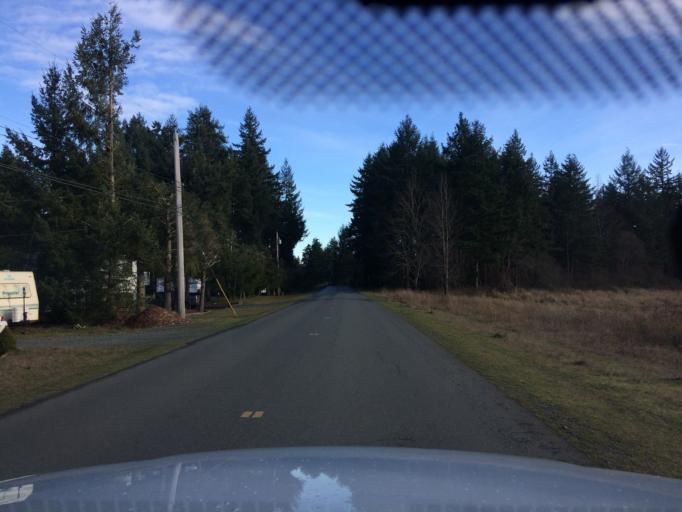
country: CA
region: British Columbia
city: Campbell River
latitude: 49.8882
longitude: -125.1311
